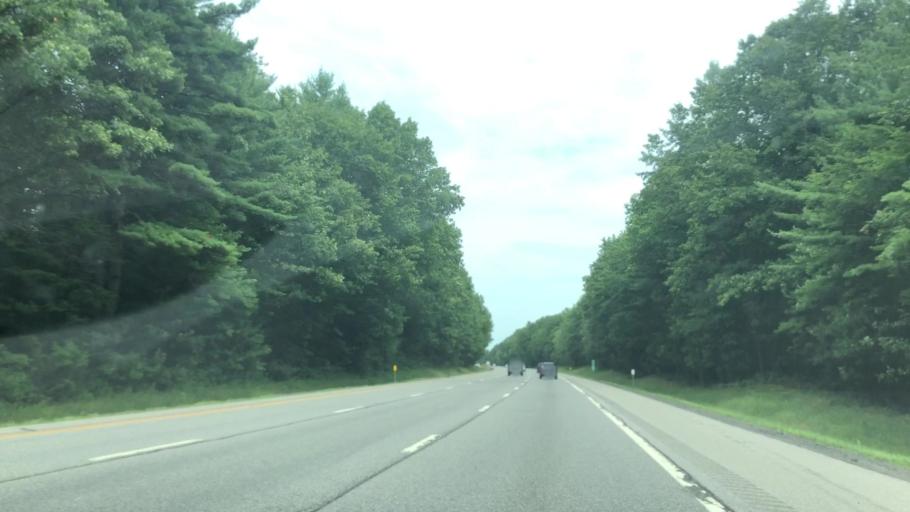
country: US
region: New York
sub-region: Saratoga County
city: Saratoga Springs
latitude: 43.1350
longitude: -73.7316
